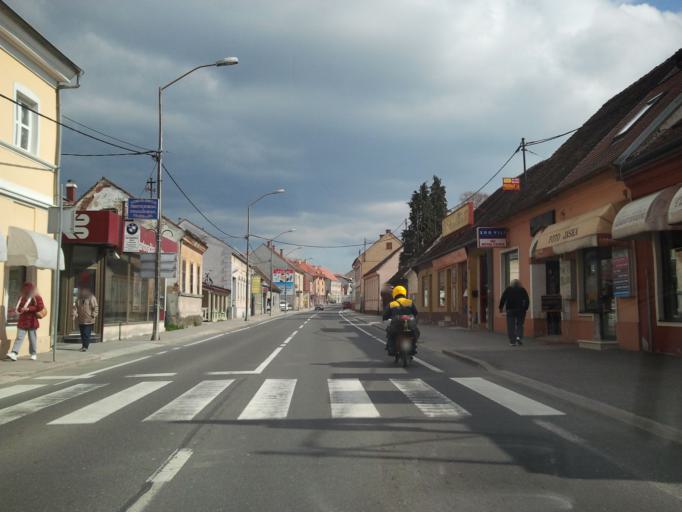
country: HR
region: Zagrebacka
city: Jastrebarsko
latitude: 45.6696
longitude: 15.6488
